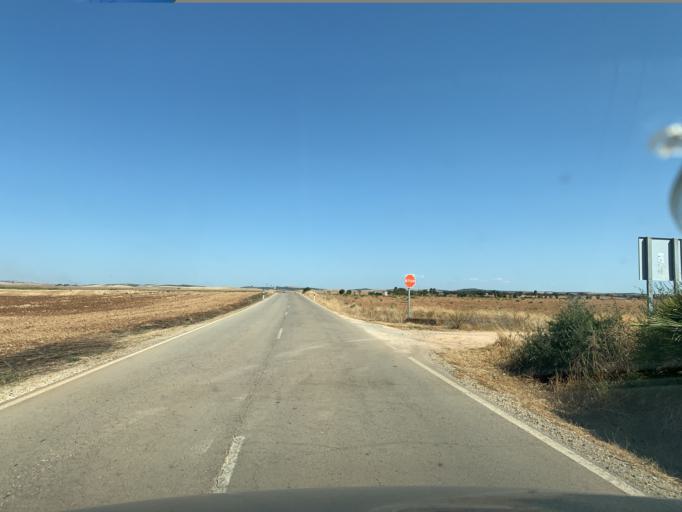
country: ES
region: Andalusia
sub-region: Provincia de Sevilla
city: La Lantejuela
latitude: 37.3729
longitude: -5.1586
